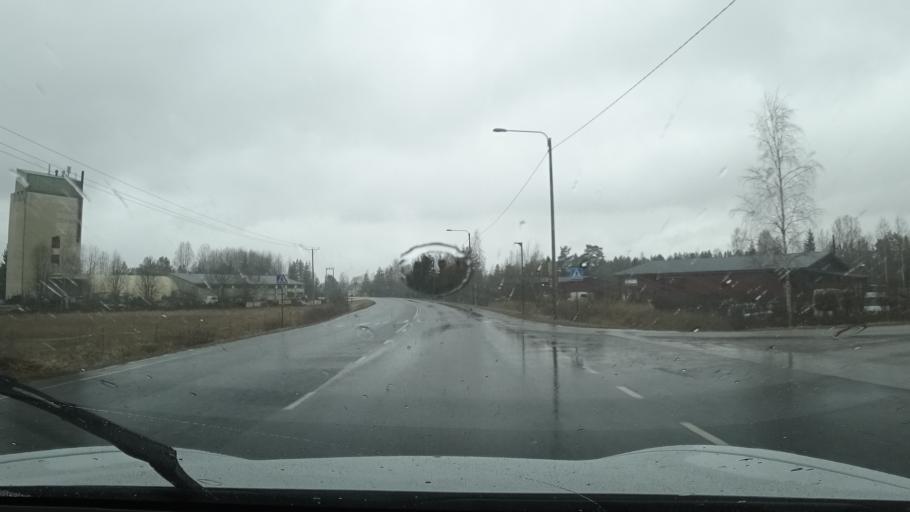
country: FI
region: Paijanne Tavastia
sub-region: Lahti
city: Orimattila
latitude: 60.8018
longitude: 25.7693
